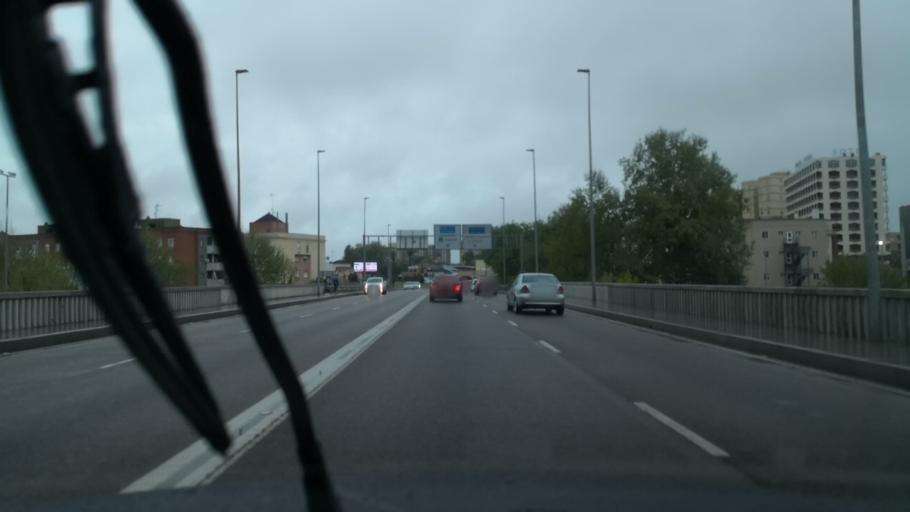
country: ES
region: Extremadura
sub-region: Provincia de Badajoz
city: Badajoz
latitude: 38.8823
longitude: -6.9840
